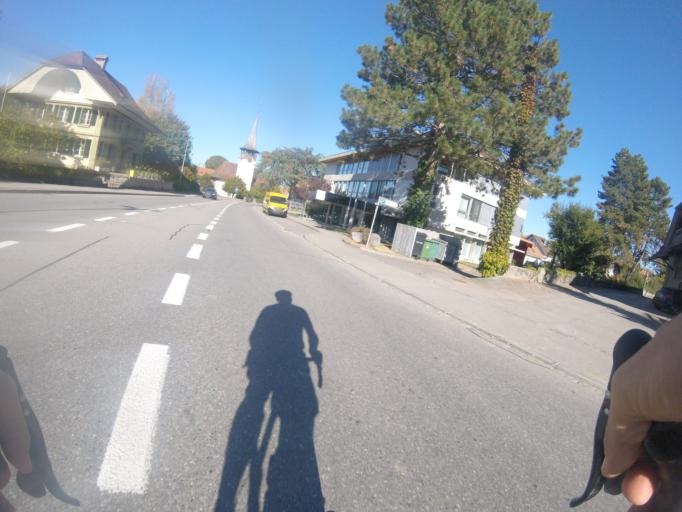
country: CH
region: Bern
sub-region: Seeland District
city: Schupfen
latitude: 47.0374
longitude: 7.3761
